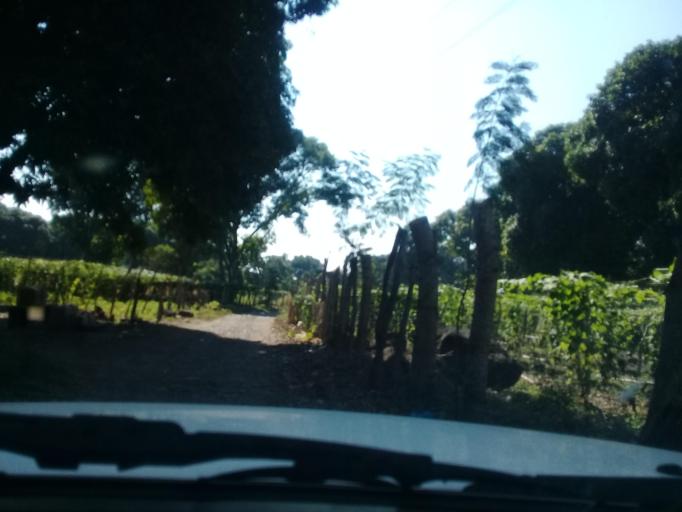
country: MX
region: Veracruz
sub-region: Emiliano Zapata
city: Plan del Rio
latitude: 19.4142
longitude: -96.6184
